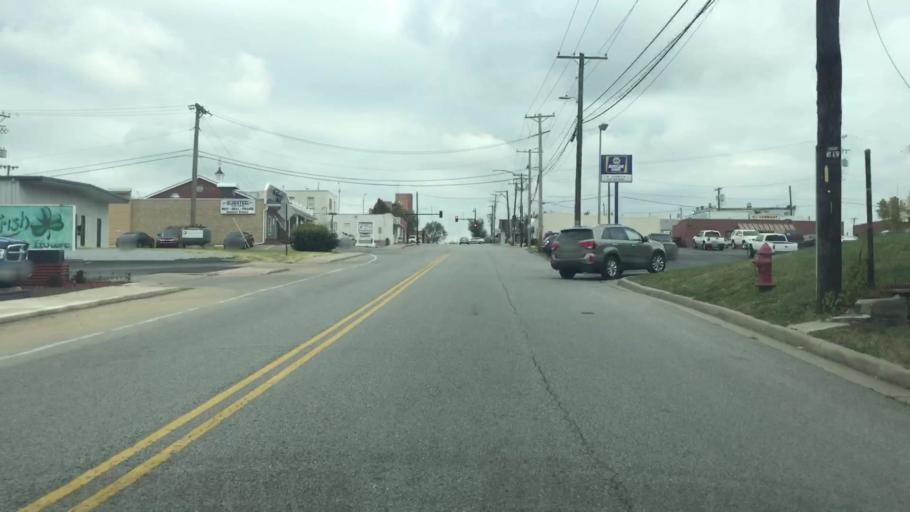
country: US
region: Missouri
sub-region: Jackson County
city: Raytown
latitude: 39.0070
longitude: -94.4635
